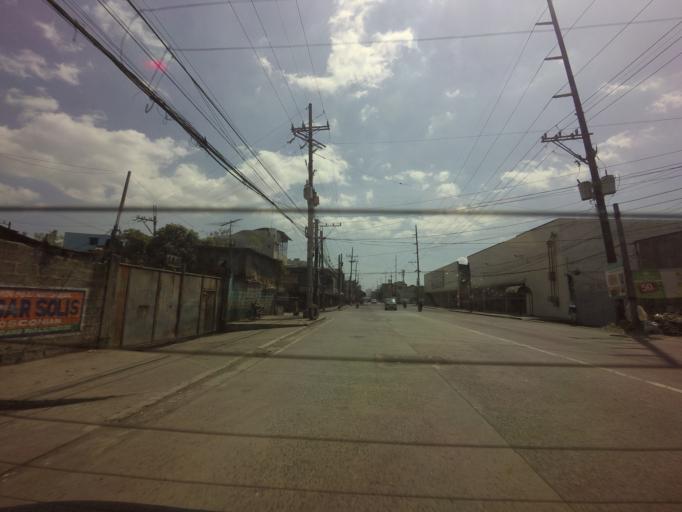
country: PH
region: Metro Manila
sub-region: Caloocan City
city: Niugan
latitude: 14.6323
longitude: 120.9636
